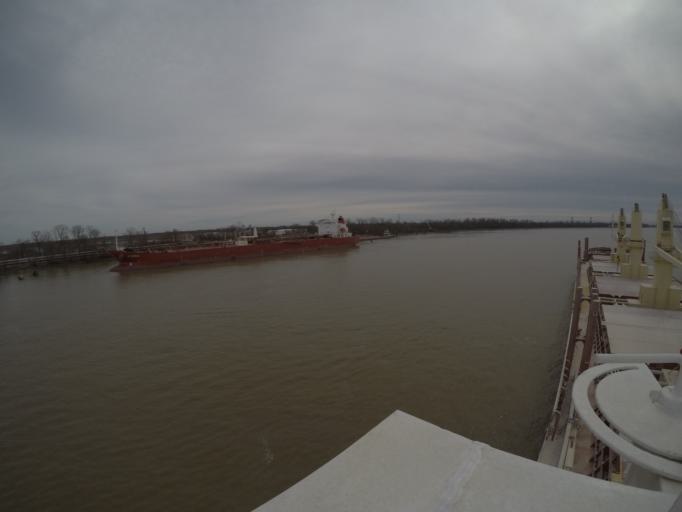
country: US
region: Louisiana
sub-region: Saint Charles Parish
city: Hahnville
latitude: 29.9836
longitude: -90.3991
